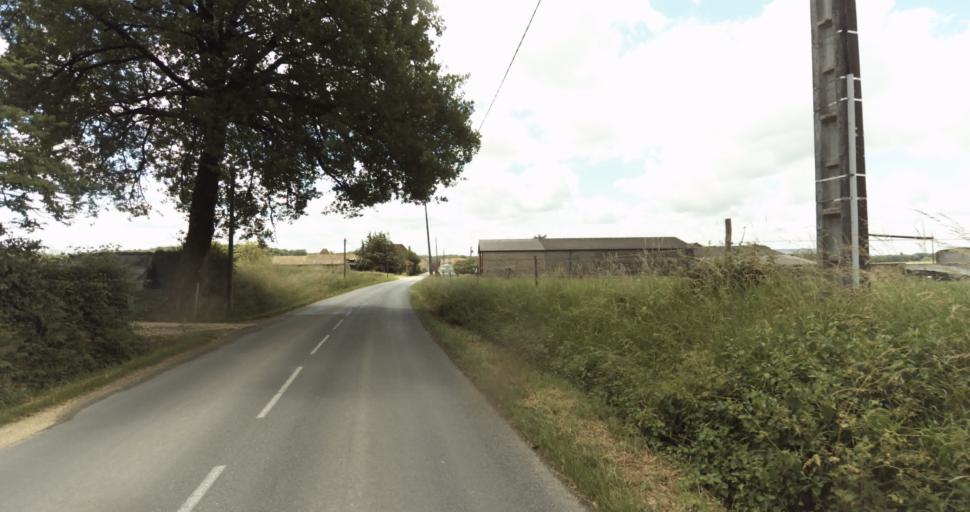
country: FR
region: Aquitaine
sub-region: Departement de la Dordogne
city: Beaumont-du-Perigord
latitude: 44.7276
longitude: 0.7578
